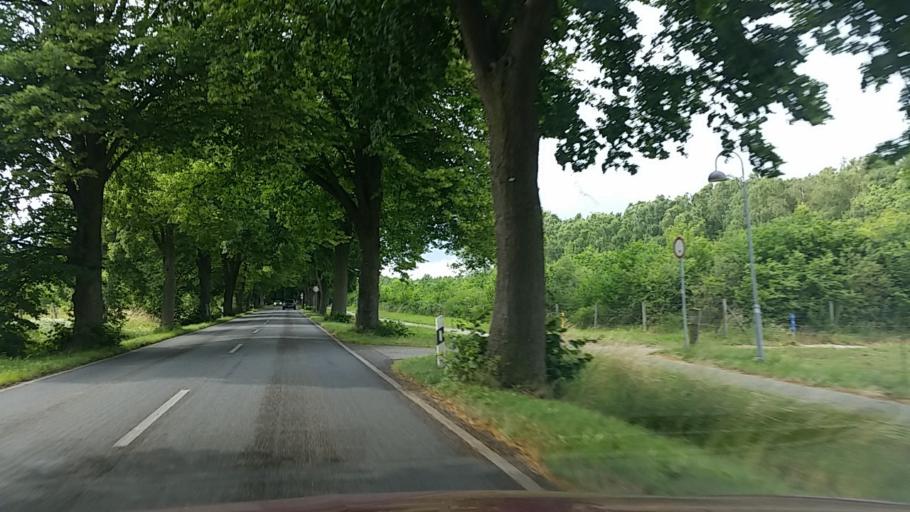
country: DE
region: Mecklenburg-Vorpommern
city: Ostseebad Kuhlungsborn
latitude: 54.1361
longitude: 11.7830
